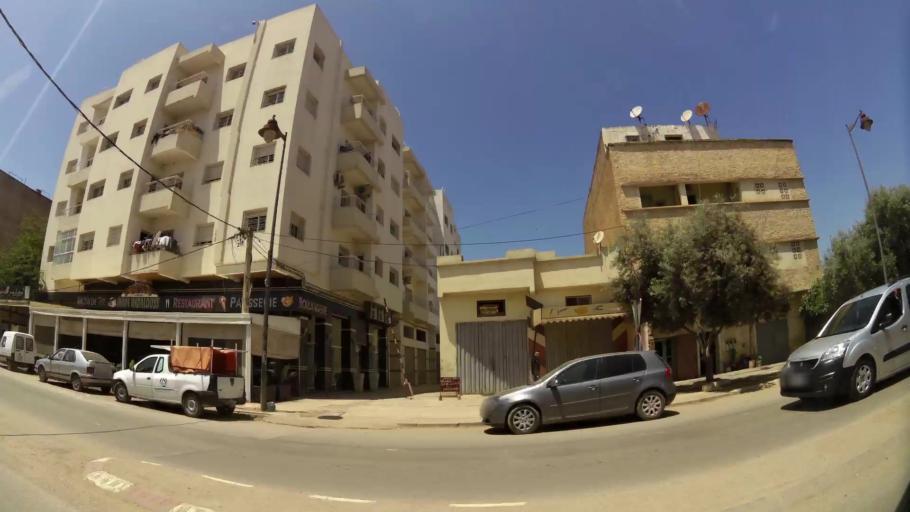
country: MA
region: Fes-Boulemane
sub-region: Fes
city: Fes
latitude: 34.0238
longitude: -5.0367
